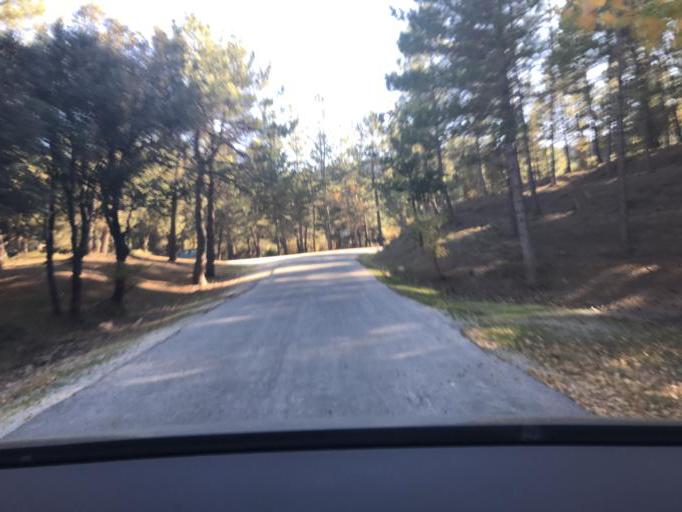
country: ES
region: Andalusia
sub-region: Provincia de Granada
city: Beas de Granada
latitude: 37.2961
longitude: -3.4732
